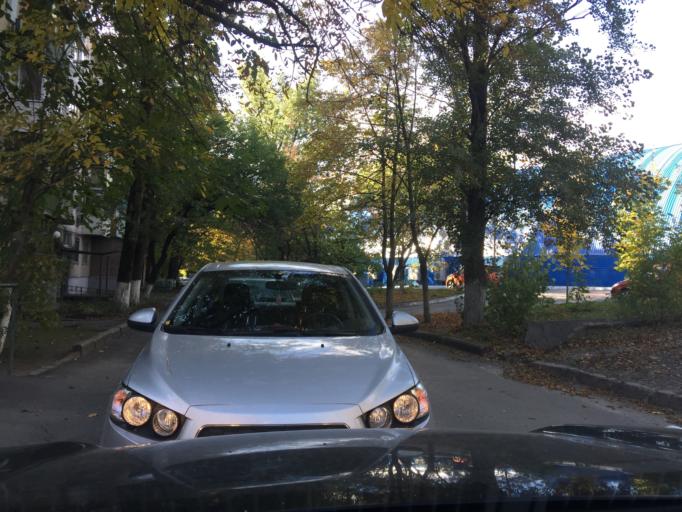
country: RU
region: Rostov
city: Rostov-na-Donu
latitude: 47.2018
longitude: 39.6215
